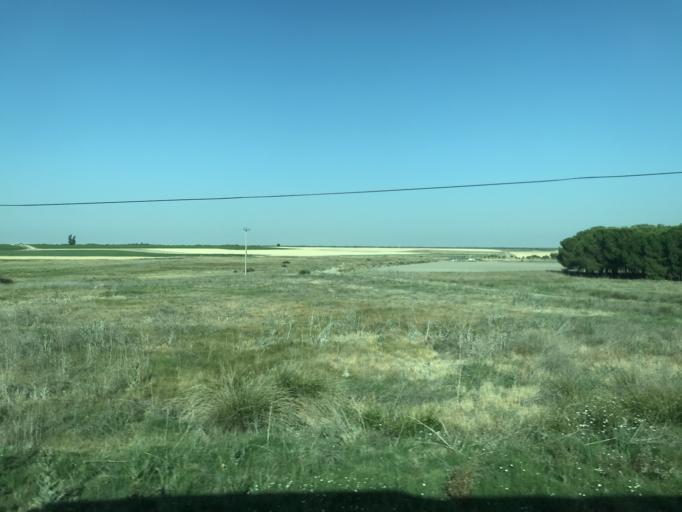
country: ES
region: Castille and Leon
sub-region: Provincia de Valladolid
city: Puras
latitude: 41.1890
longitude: -4.6606
